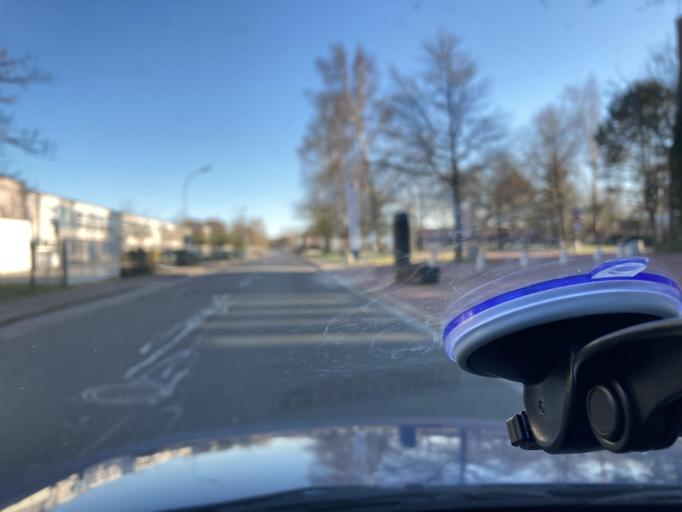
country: DE
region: Schleswig-Holstein
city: Heide
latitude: 54.2084
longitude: 9.0988
